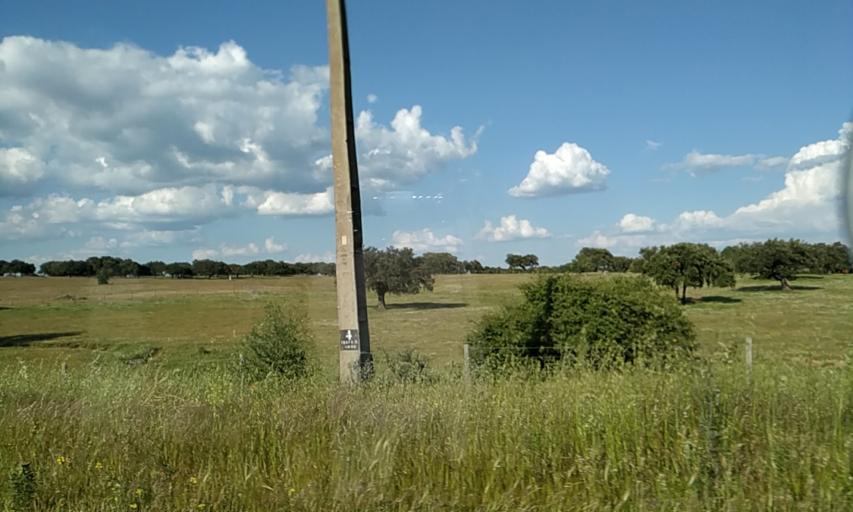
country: PT
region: Portalegre
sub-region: Portalegre
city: Urra
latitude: 39.1384
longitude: -7.4501
